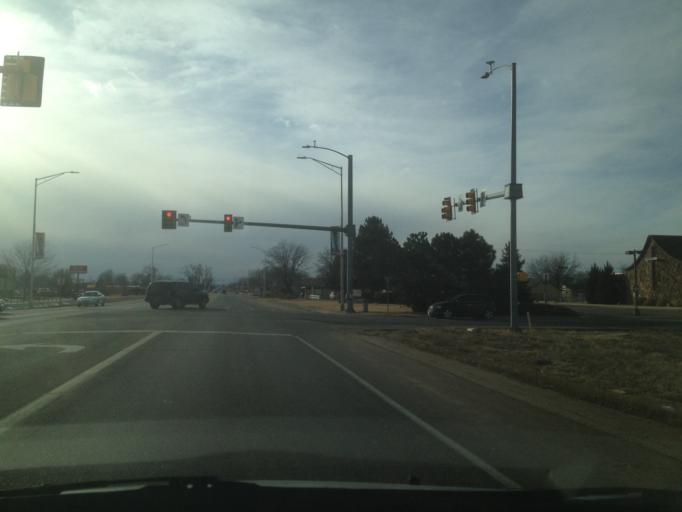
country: US
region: Colorado
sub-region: Weld County
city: Fort Lupton
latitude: 40.0803
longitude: -104.8043
